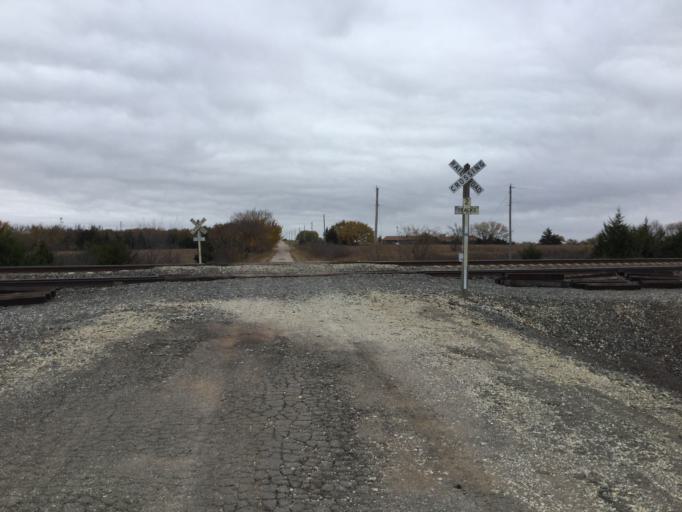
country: US
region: Kansas
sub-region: Butler County
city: El Dorado
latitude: 37.9207
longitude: -96.7676
